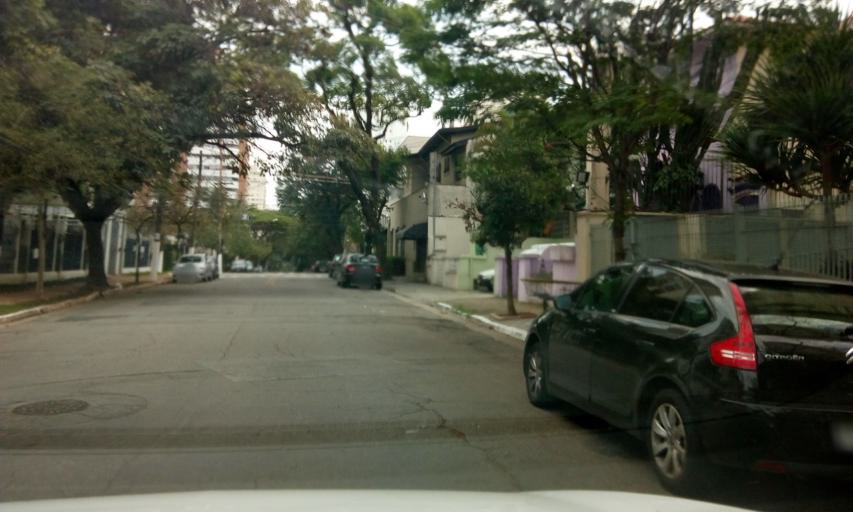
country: BR
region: Sao Paulo
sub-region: Sao Paulo
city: Sao Paulo
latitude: -23.6101
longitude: -46.6569
